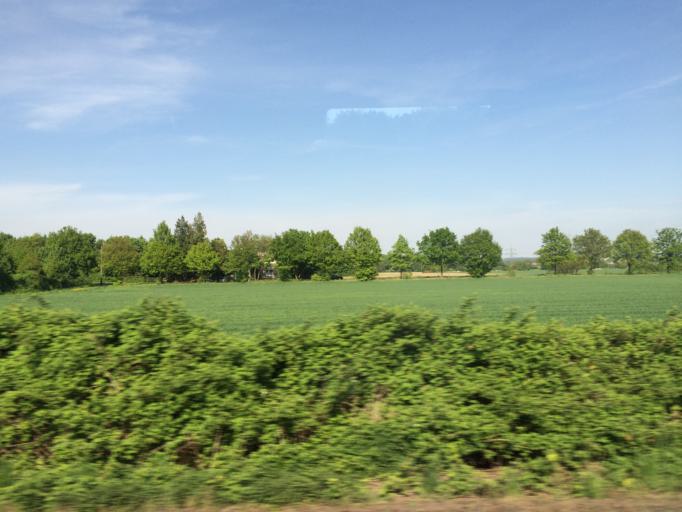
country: DE
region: North Rhine-Westphalia
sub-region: Regierungsbezirk Dusseldorf
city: Langenfeld
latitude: 51.1279
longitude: 6.9134
